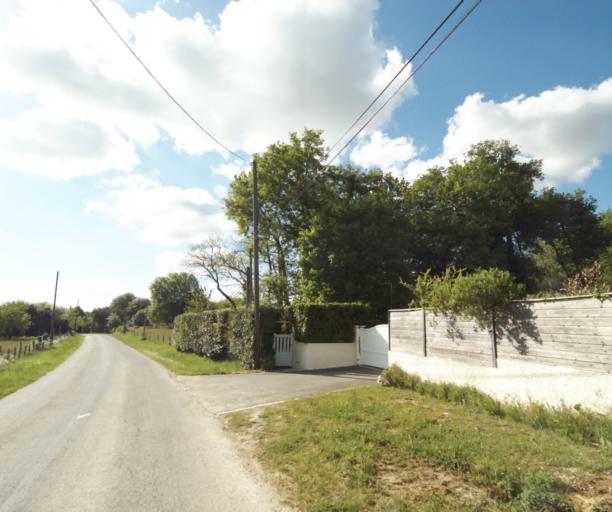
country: FR
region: Poitou-Charentes
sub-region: Departement de la Charente-Maritime
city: Nieul-les-Saintes
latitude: 45.7123
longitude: -0.7239
